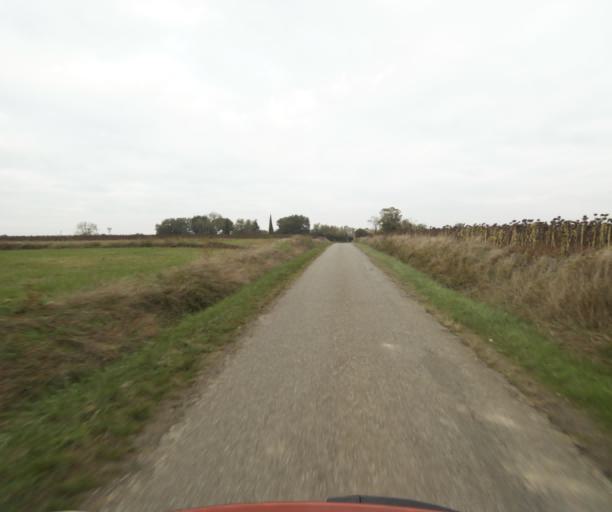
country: FR
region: Midi-Pyrenees
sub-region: Departement du Tarn-et-Garonne
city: Verdun-sur-Garonne
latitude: 43.8199
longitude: 1.2070
